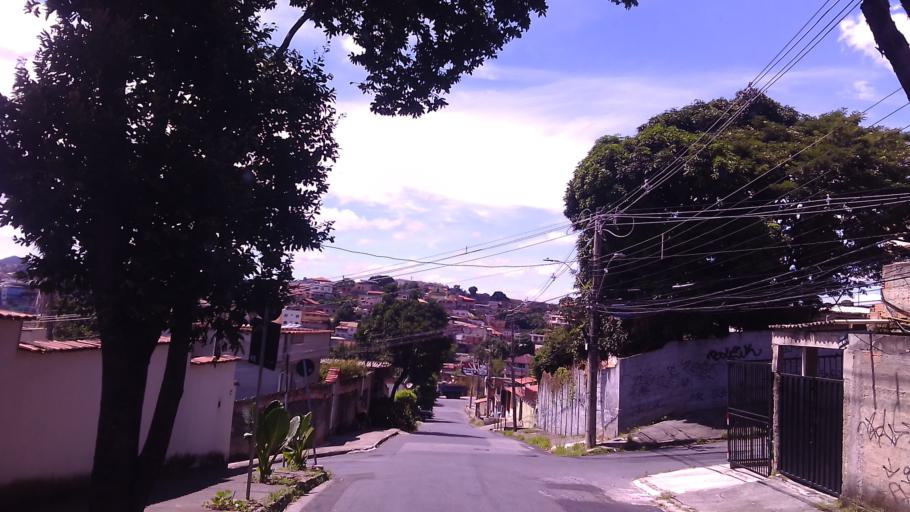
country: BR
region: Minas Gerais
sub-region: Belo Horizonte
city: Belo Horizonte
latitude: -19.8591
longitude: -43.9072
